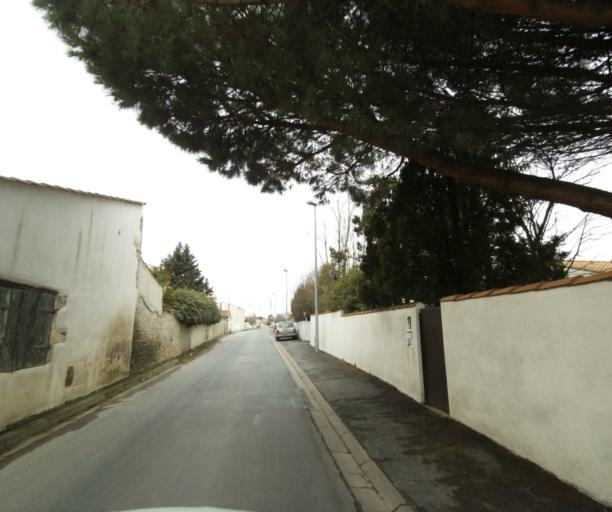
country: FR
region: Poitou-Charentes
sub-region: Departement de la Charente-Maritime
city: Lagord
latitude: 46.1921
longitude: -1.1522
